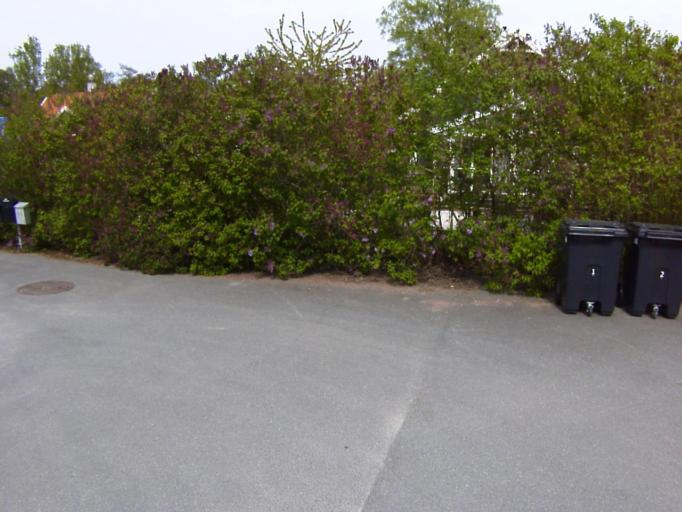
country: SE
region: Skane
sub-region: Kristianstads Kommun
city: Kristianstad
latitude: 56.0751
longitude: 14.2095
